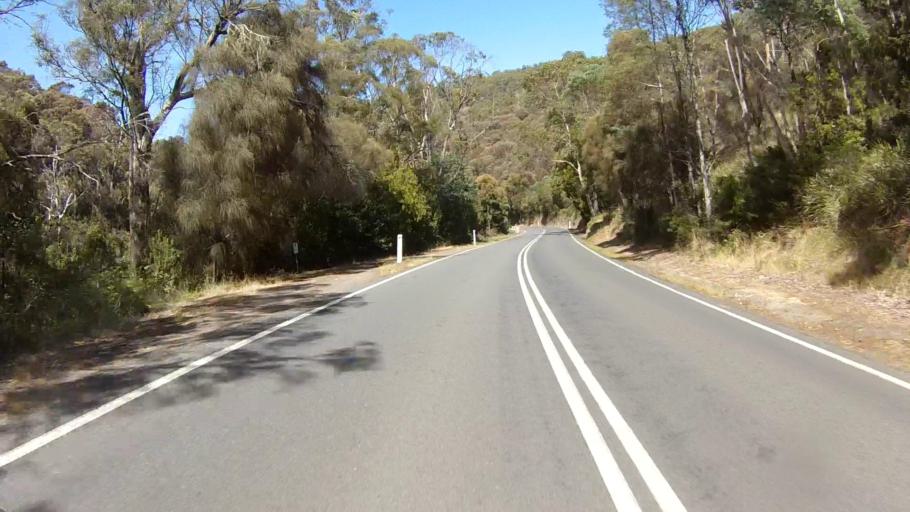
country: AU
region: Tasmania
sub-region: Derwent Valley
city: New Norfolk
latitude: -42.6800
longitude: 146.7664
